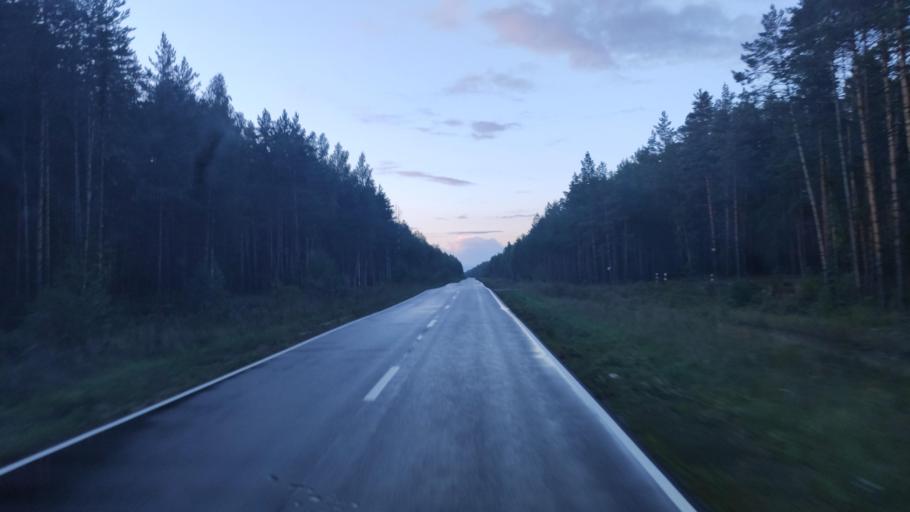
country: RU
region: Vladimir
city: Galitsy
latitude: 56.0476
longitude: 42.8640
